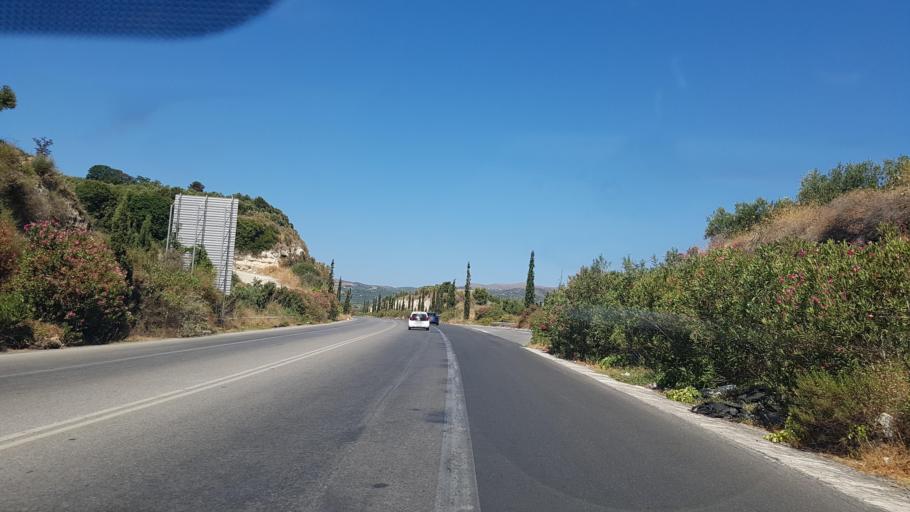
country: GR
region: Crete
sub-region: Nomos Chanias
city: Kolympari
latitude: 35.5230
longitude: 23.8120
